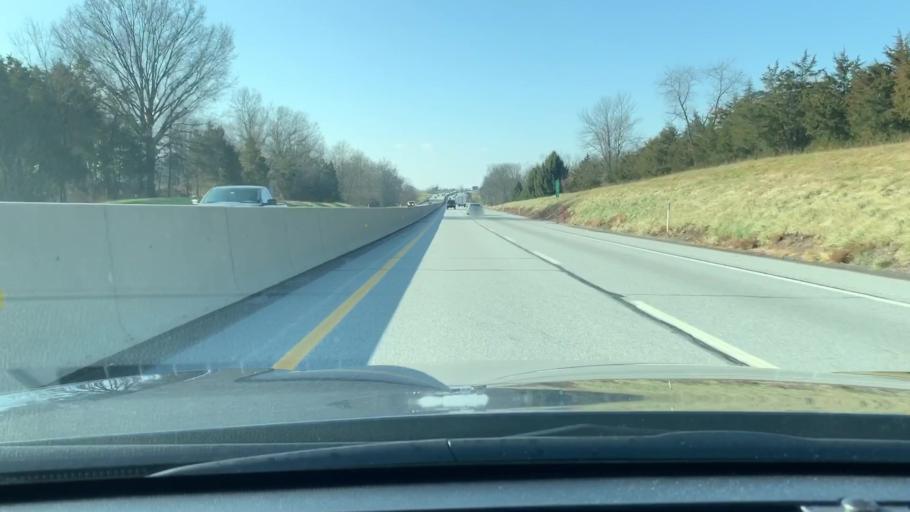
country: US
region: Pennsylvania
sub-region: Lancaster County
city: Elizabethtown
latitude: 40.2094
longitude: -76.5564
